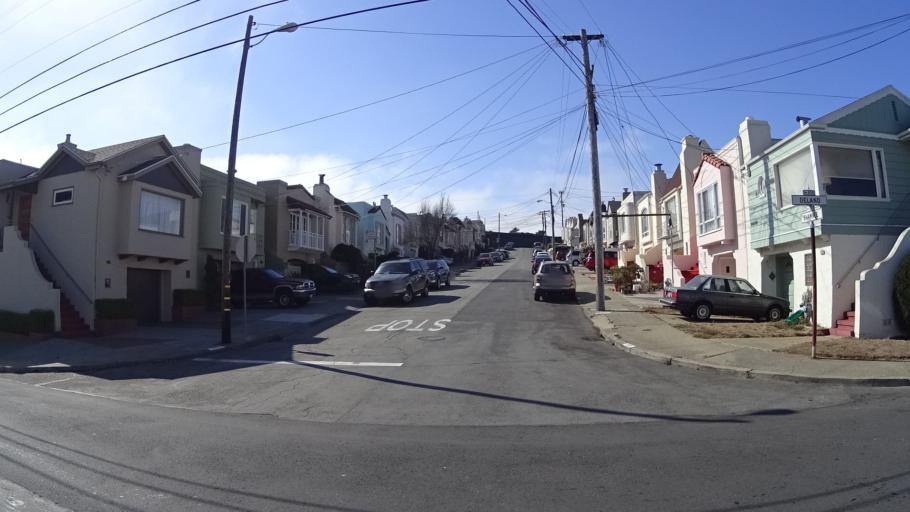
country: US
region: California
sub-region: San Mateo County
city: Daly City
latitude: 37.7183
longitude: -122.4462
